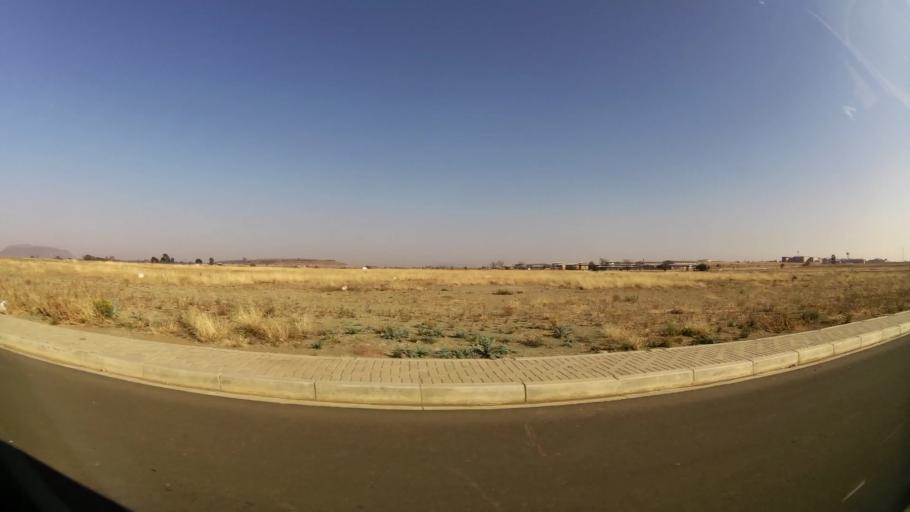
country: ZA
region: Orange Free State
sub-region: Mangaung Metropolitan Municipality
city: Bloemfontein
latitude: -29.1919
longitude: 26.2185
